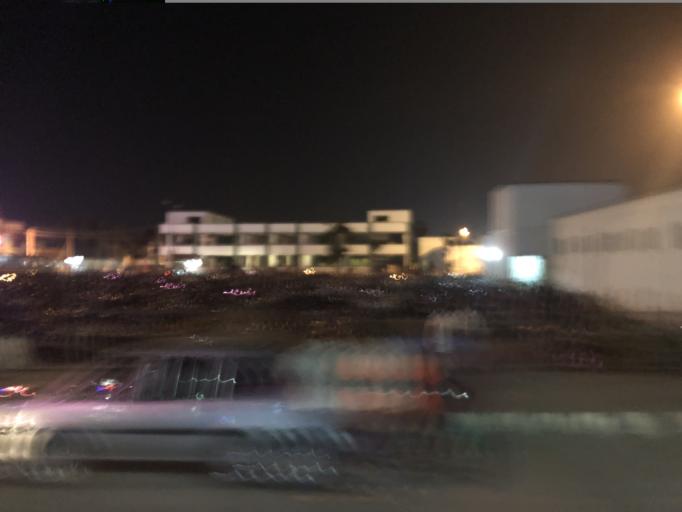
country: IN
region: Tamil Nadu
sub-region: Thanjavur
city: Thanjavur
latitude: 10.7493
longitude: 79.1127
